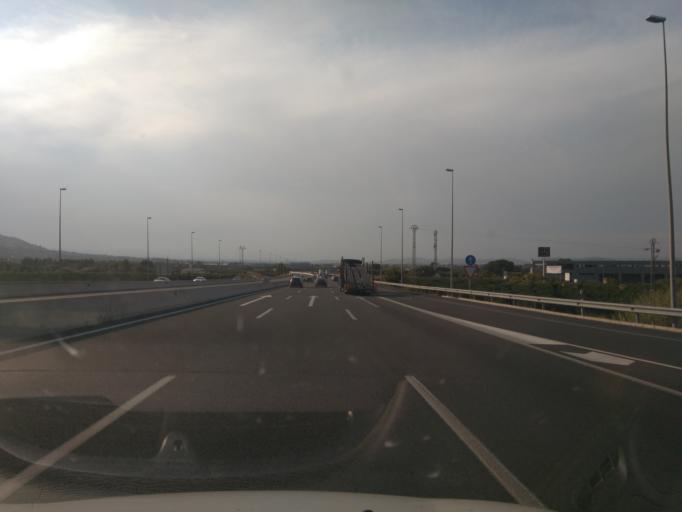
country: ES
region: Valencia
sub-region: Provincia de Valencia
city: Torrent
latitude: 39.4181
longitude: -0.5108
